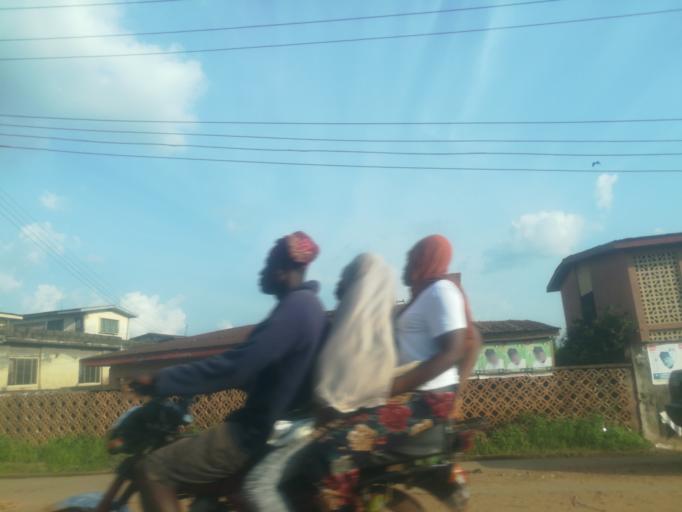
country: NG
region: Oyo
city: Ibadan
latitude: 7.3807
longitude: 3.8203
